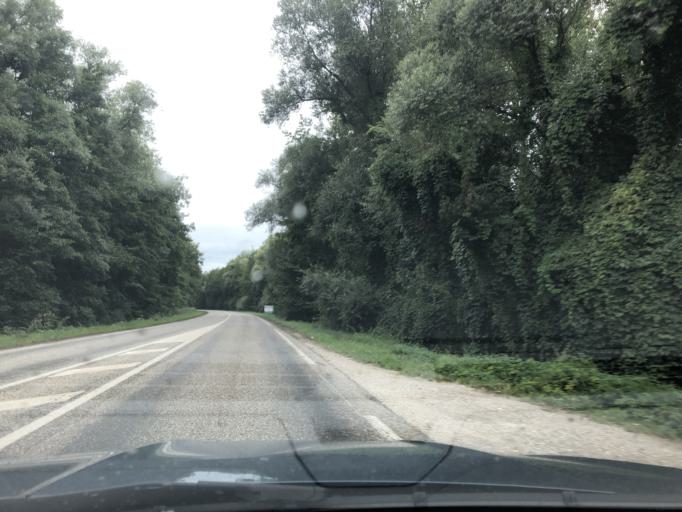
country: DE
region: Rheinland-Pfalz
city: Berg
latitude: 48.9701
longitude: 8.1801
